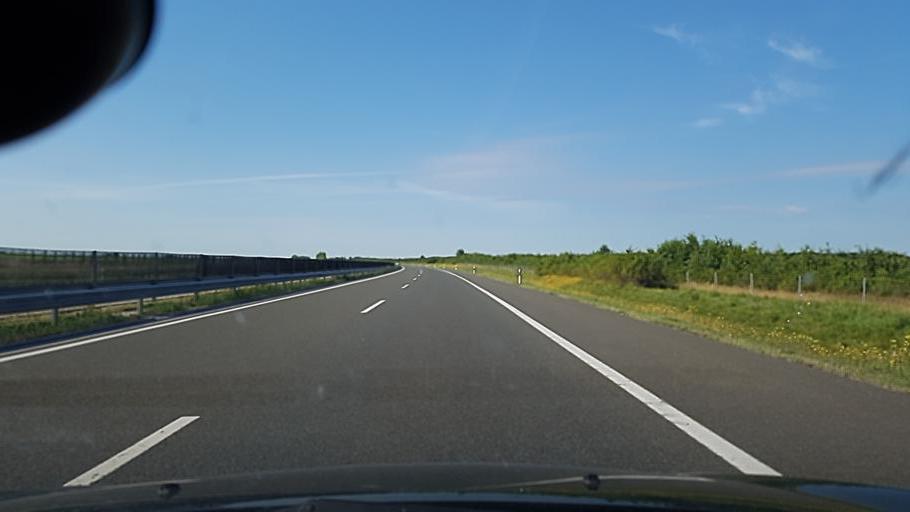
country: HU
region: Fejer
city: Baracs
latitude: 46.8936
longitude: 18.8770
